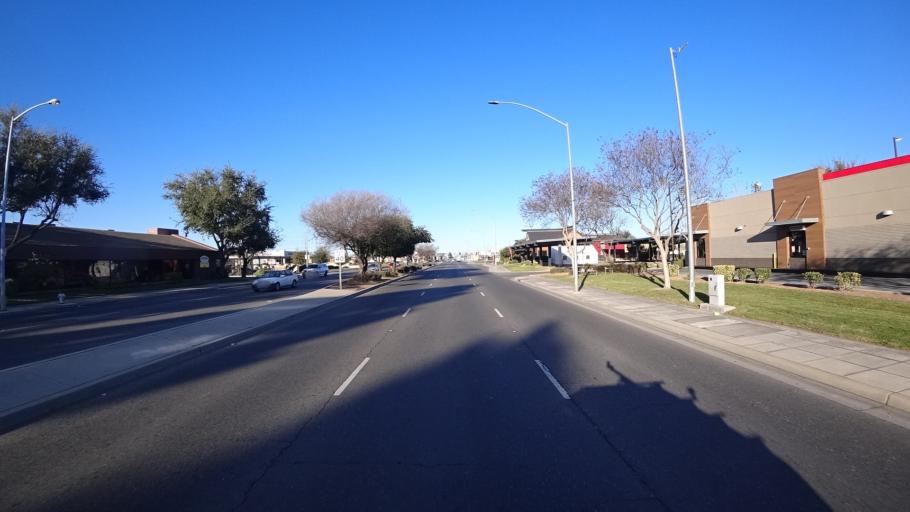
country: US
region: California
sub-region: Fresno County
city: West Park
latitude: 36.8083
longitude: -119.8544
